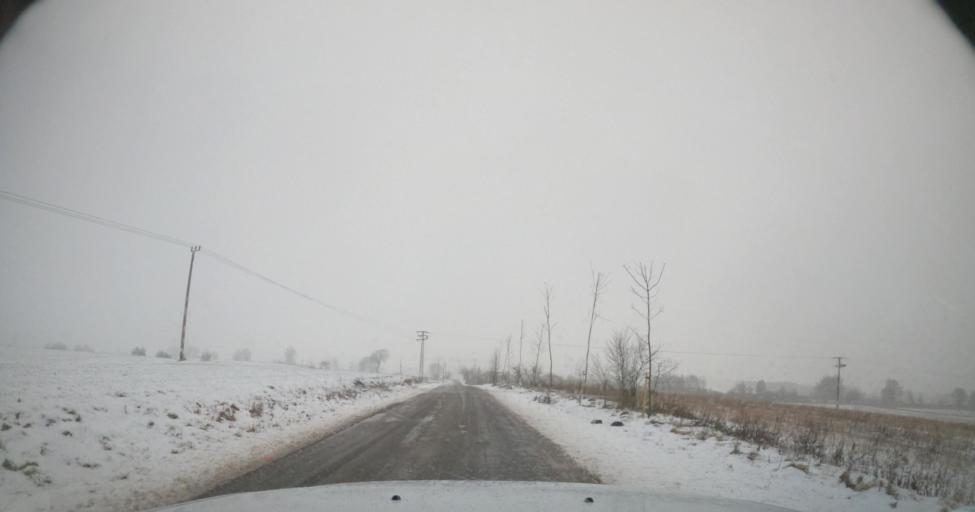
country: PL
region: West Pomeranian Voivodeship
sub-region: Powiat kamienski
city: Golczewo
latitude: 53.7909
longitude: 14.9518
